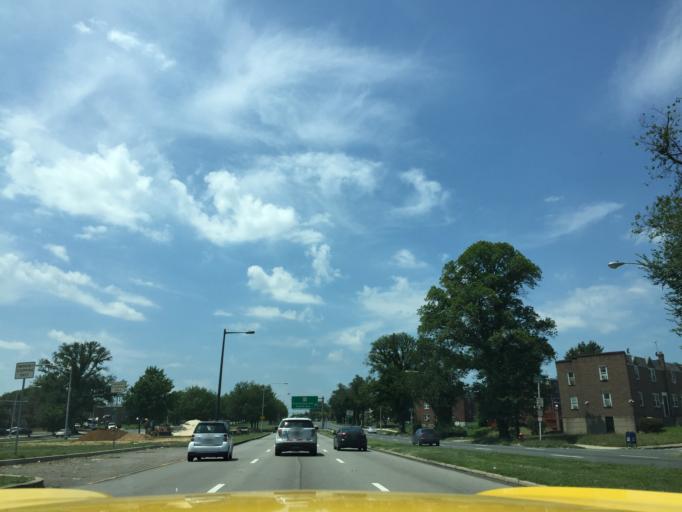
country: US
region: Pennsylvania
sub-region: Montgomery County
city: Rockledge
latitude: 40.0341
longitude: -75.0755
